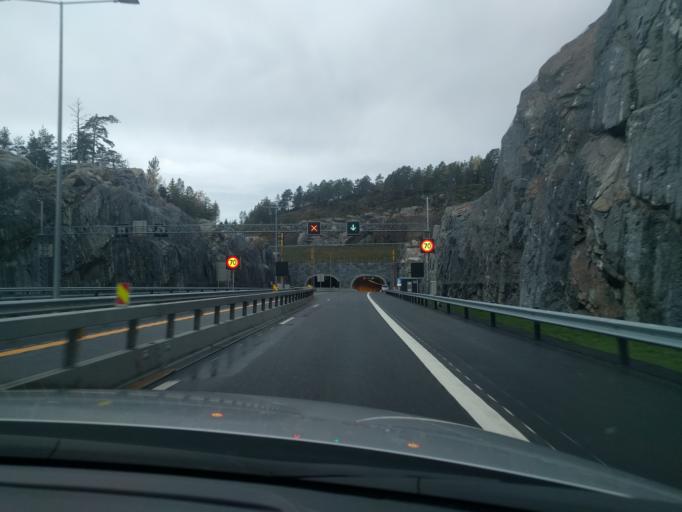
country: NO
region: Vestfold
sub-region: Larvik
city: Larvik
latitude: 59.0813
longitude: 10.0533
